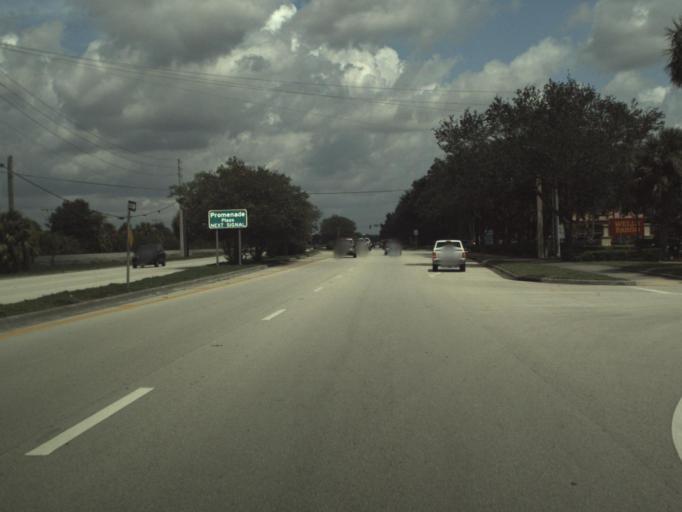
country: US
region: Florida
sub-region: Palm Beach County
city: North Palm Beach
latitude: 26.8198
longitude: -80.0837
